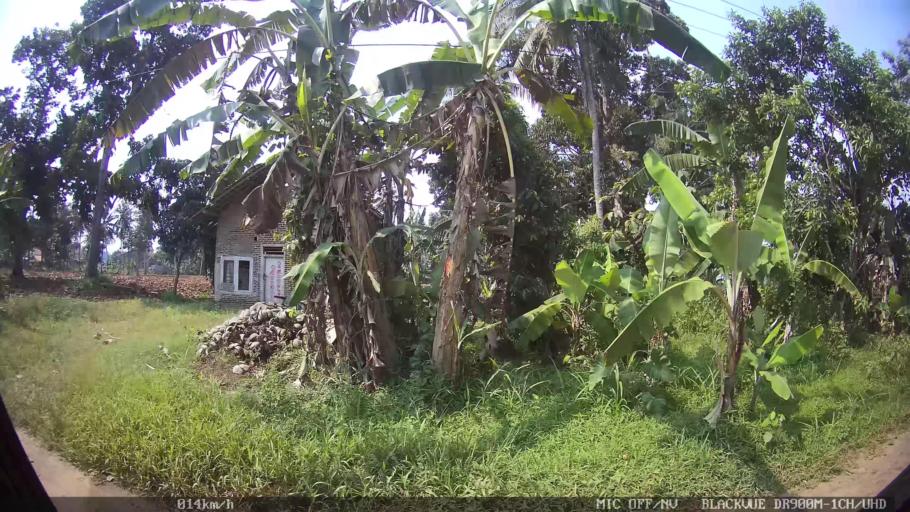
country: ID
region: Lampung
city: Natar
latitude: -5.2941
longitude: 105.2421
